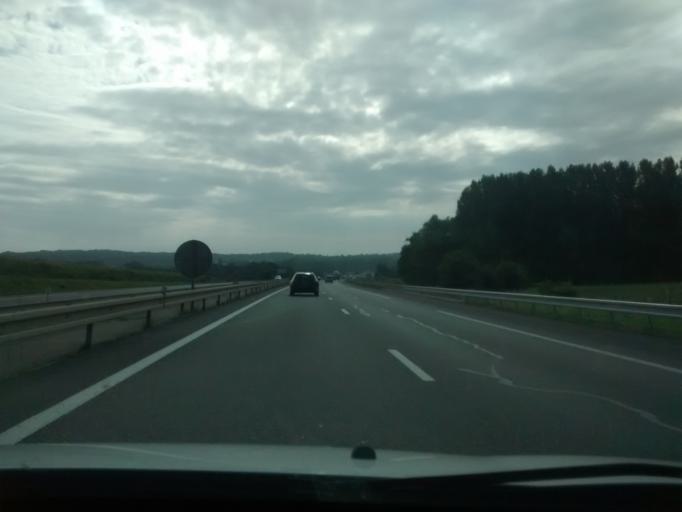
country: FR
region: Pays de la Loire
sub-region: Departement de la Mayenne
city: Saint-Pierre-la-Cour
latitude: 48.0827
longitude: -1.0143
